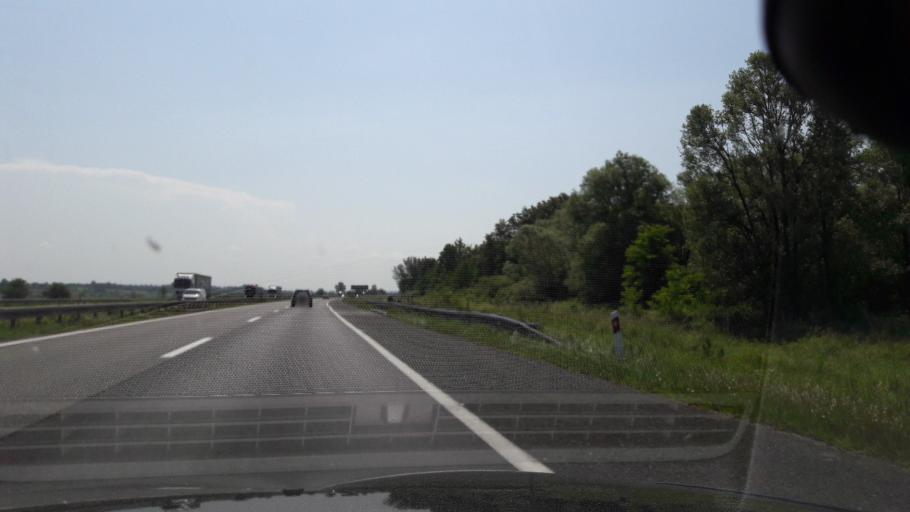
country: HR
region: Zagrebacka
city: Kriz
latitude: 45.6786
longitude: 16.4676
